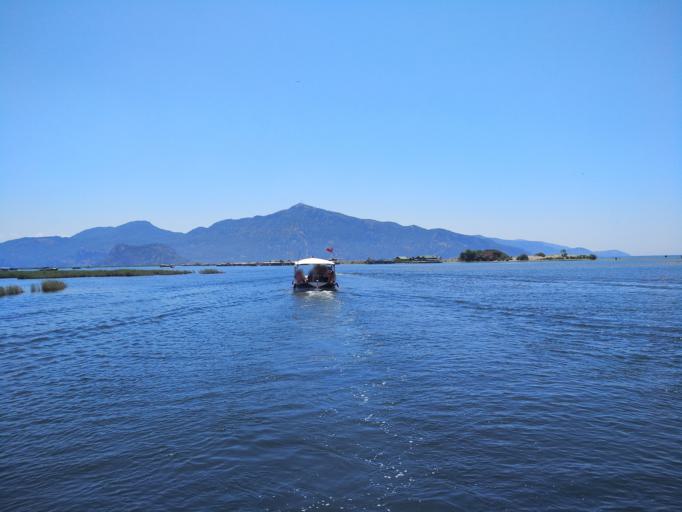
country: TR
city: Dalyan
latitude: 36.8049
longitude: 28.6041
